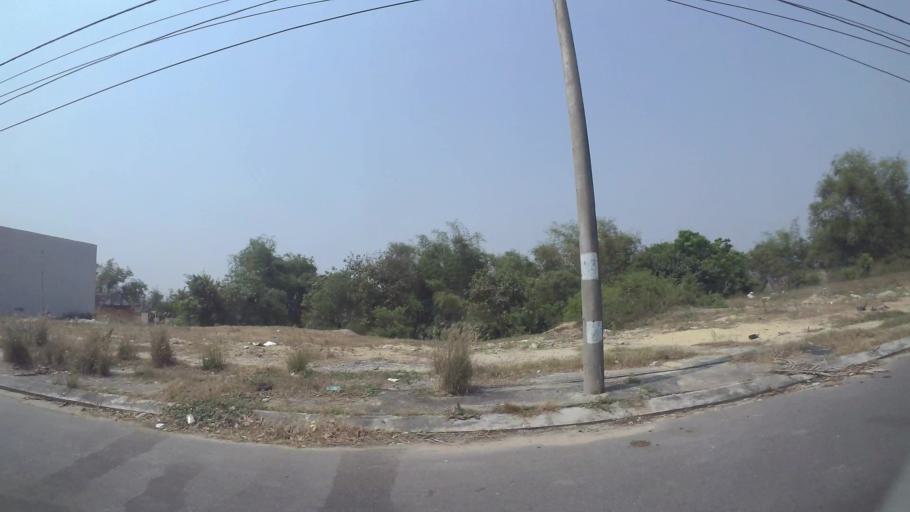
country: VN
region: Da Nang
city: Ngu Hanh Son
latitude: 16.0118
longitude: 108.2519
